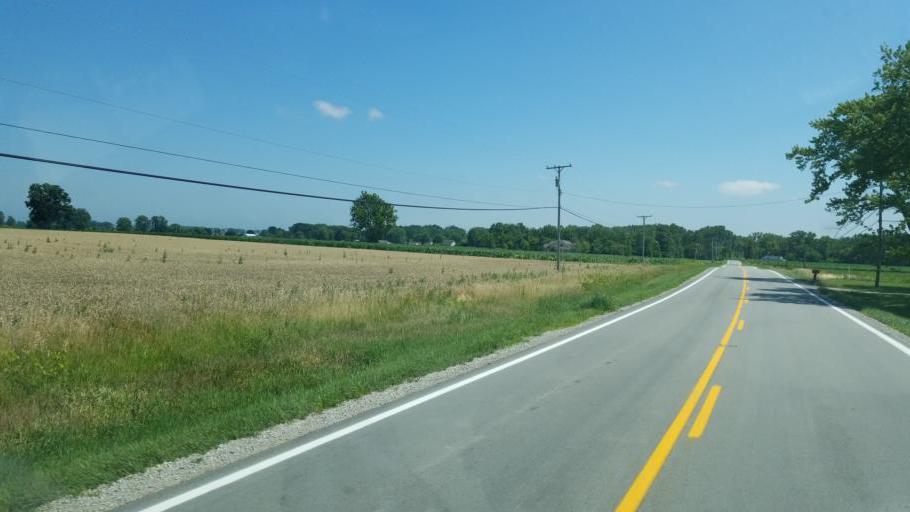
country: US
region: Ohio
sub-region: Erie County
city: Sandusky
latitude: 41.4315
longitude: -82.8233
